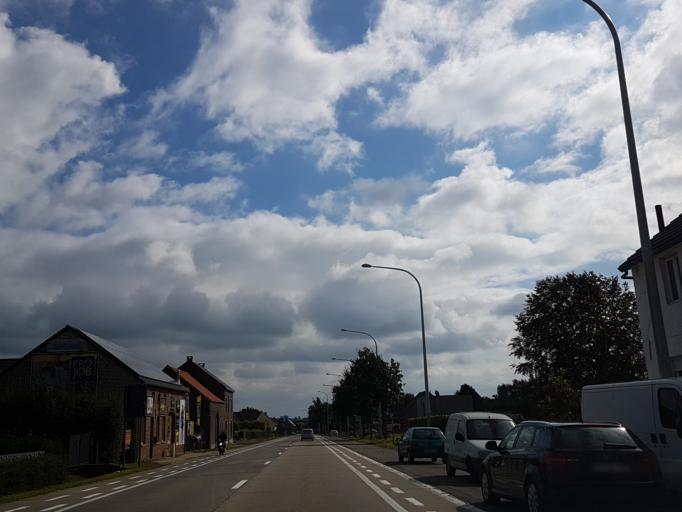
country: BE
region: Flanders
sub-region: Provincie Vlaams-Brabant
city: Boutersem
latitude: 50.8464
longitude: 4.8224
